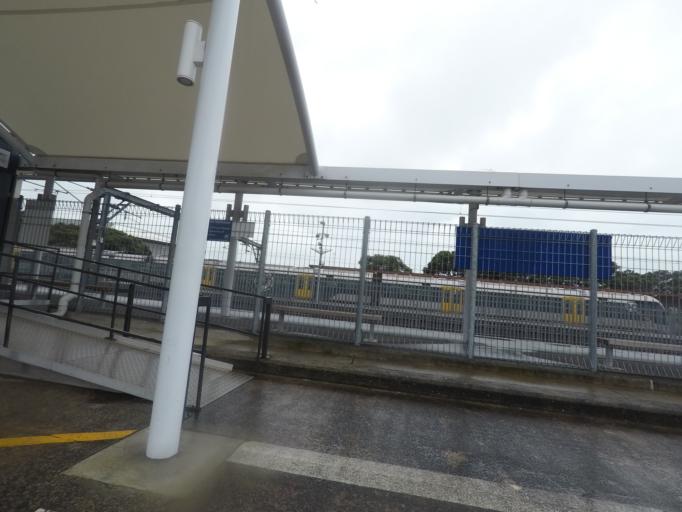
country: NZ
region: Auckland
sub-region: Auckland
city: Auckland
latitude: -36.8486
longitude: 174.7790
